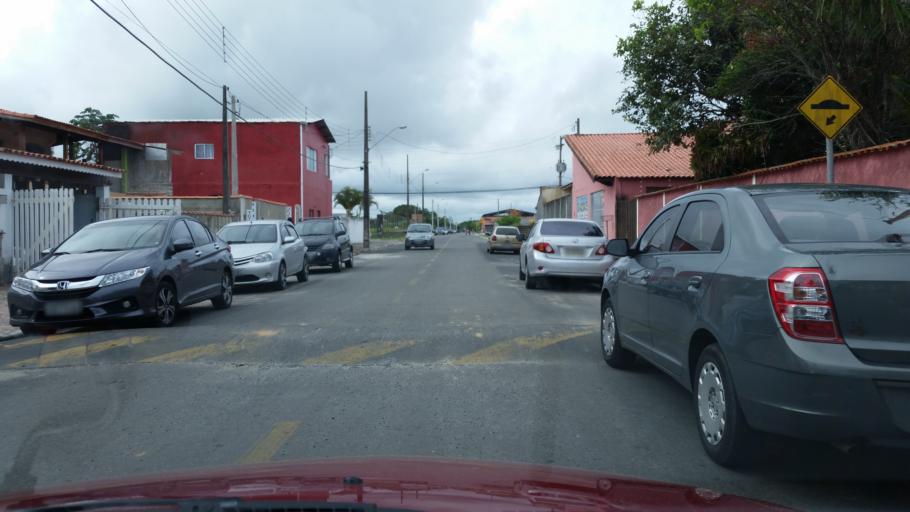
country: BR
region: Sao Paulo
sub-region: Iguape
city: Iguape
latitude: -24.7480
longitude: -47.5536
